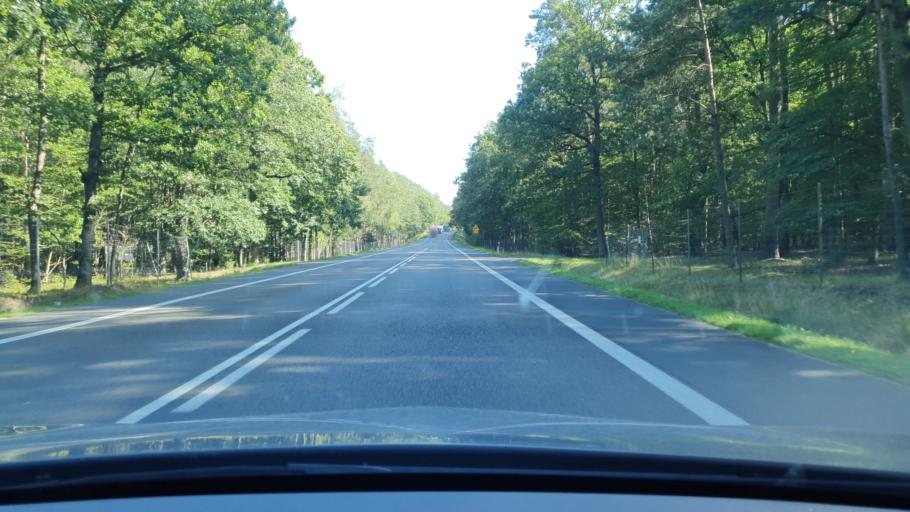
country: PL
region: West Pomeranian Voivodeship
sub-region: Powiat kamienski
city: Miedzyzdroje
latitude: 53.9006
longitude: 14.4580
